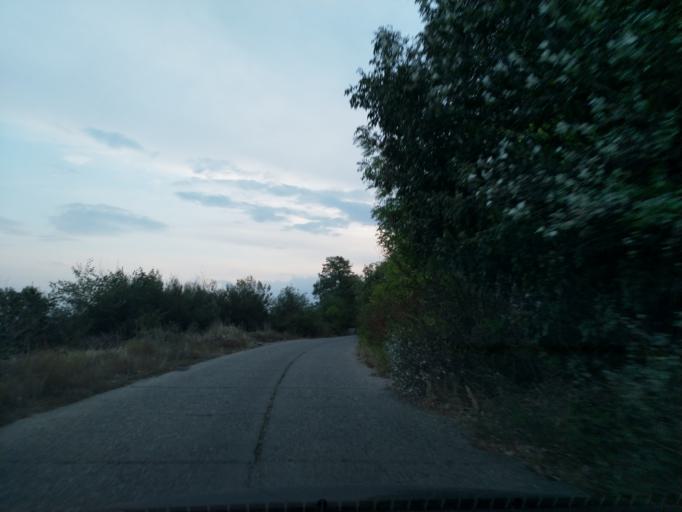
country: RS
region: Central Serbia
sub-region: Pomoravski Okrug
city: Paracin
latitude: 43.8655
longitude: 21.4549
